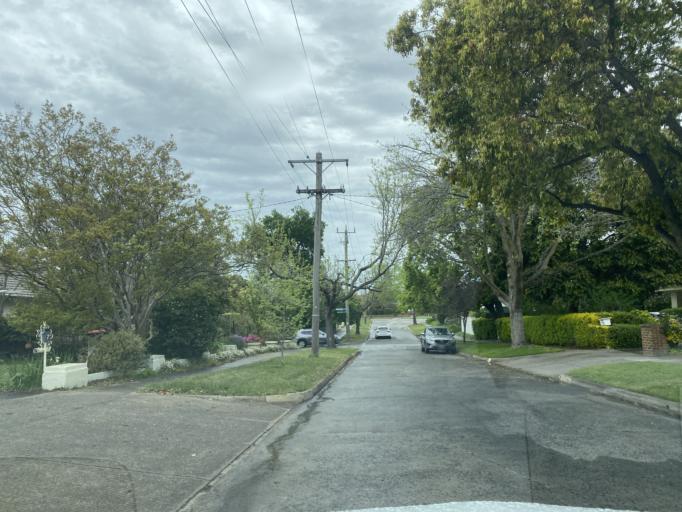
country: AU
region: Victoria
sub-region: Boroondara
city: Camberwell
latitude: -37.8404
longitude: 145.0701
